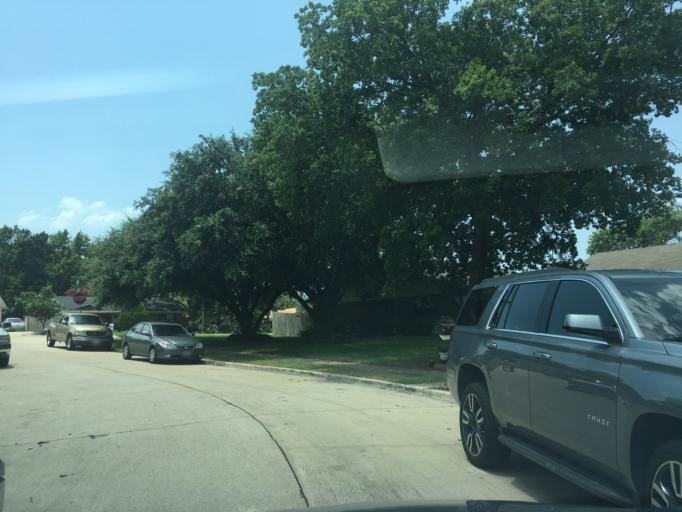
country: US
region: Texas
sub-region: Dallas County
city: Carrollton
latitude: 32.9472
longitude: -96.8781
